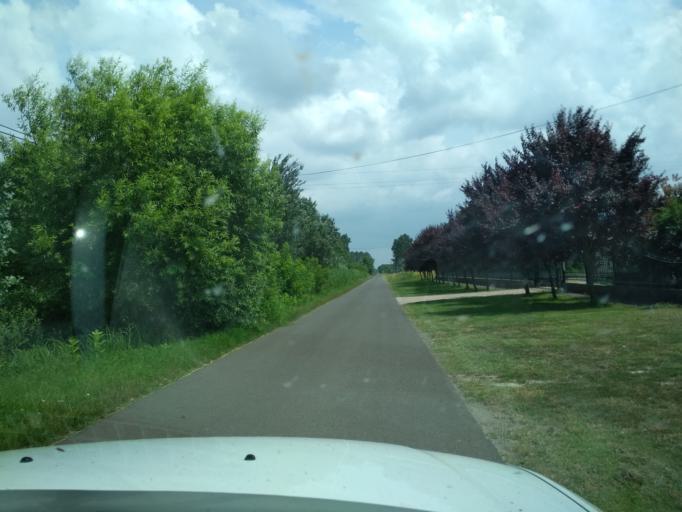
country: HU
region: Pest
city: Tapioszentmarton
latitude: 47.3274
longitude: 19.7623
